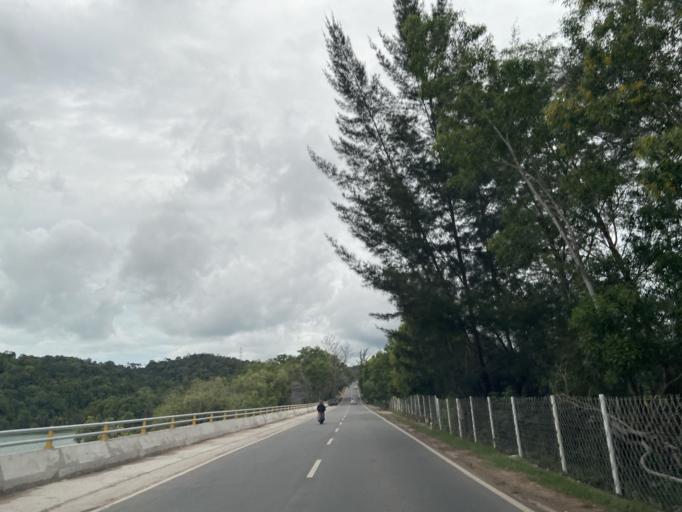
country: SG
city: Singapore
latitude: 1.1102
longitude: 104.0091
